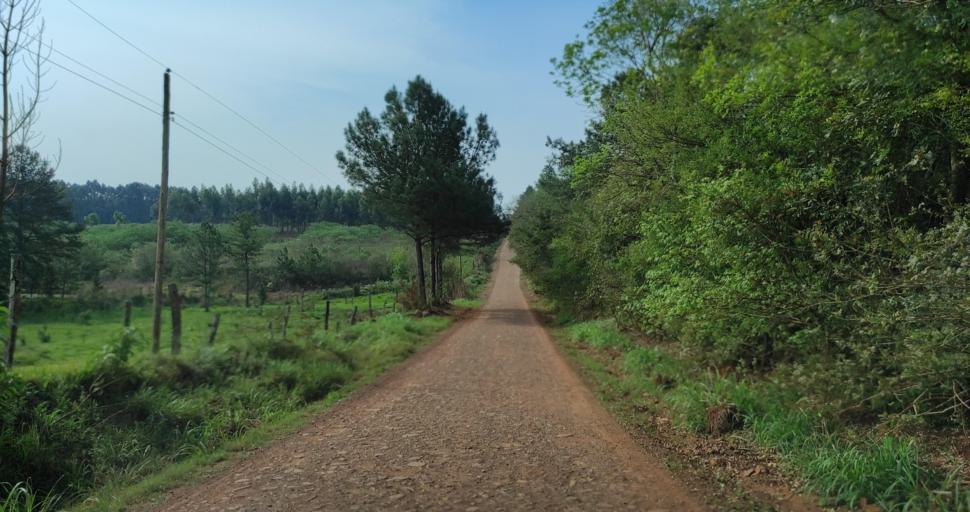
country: AR
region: Misiones
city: Garuhape
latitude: -26.8718
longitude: -55.0056
